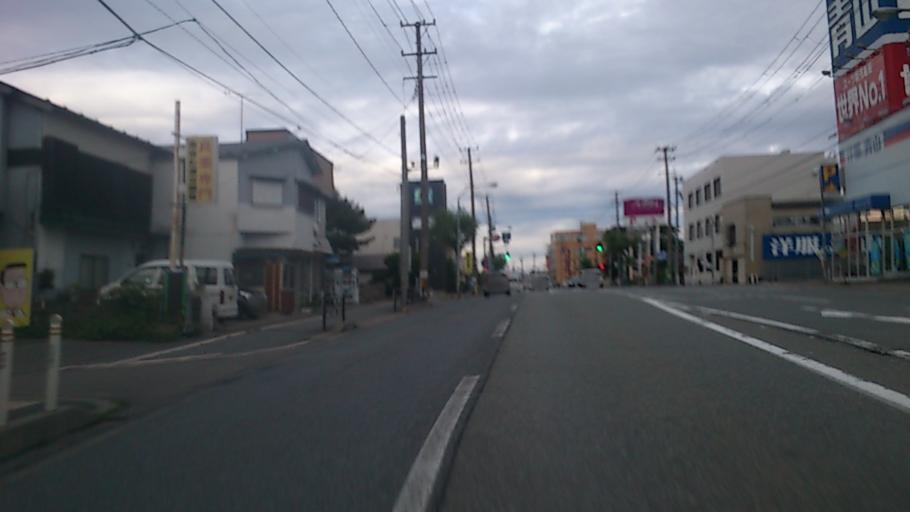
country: JP
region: Akita
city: Akita Shi
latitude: 39.7494
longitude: 140.0709
